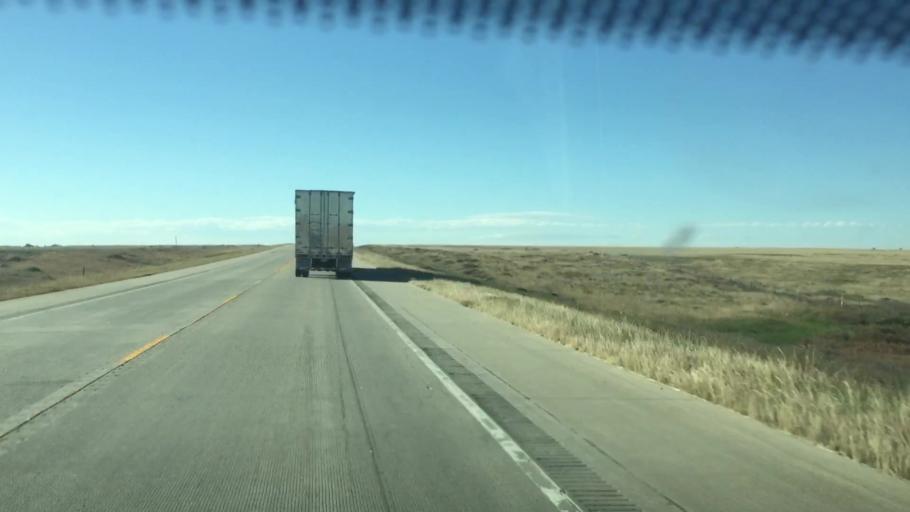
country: US
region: Colorado
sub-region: Kiowa County
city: Eads
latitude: 38.8018
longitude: -102.9598
